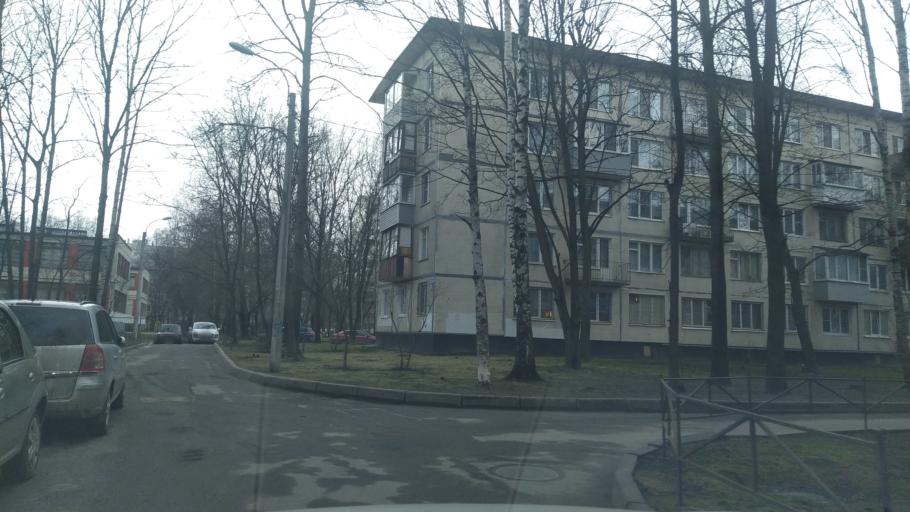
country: RU
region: St.-Petersburg
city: Grazhdanka
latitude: 60.0473
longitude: 30.3949
